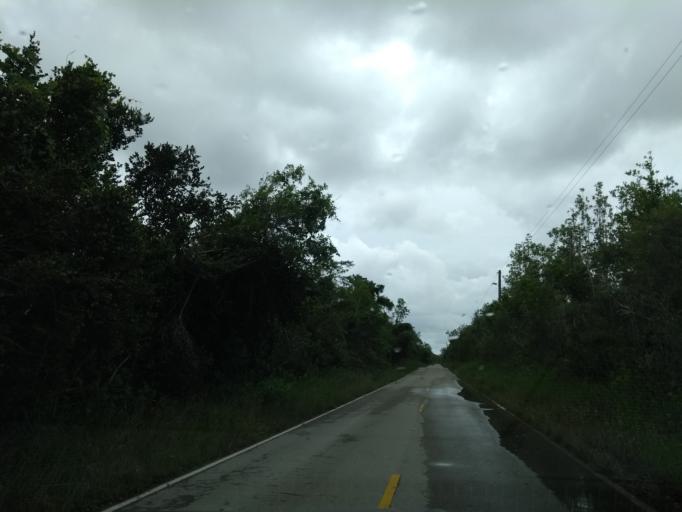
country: US
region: Florida
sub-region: Miami-Dade County
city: The Hammocks
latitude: 25.7599
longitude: -80.9249
